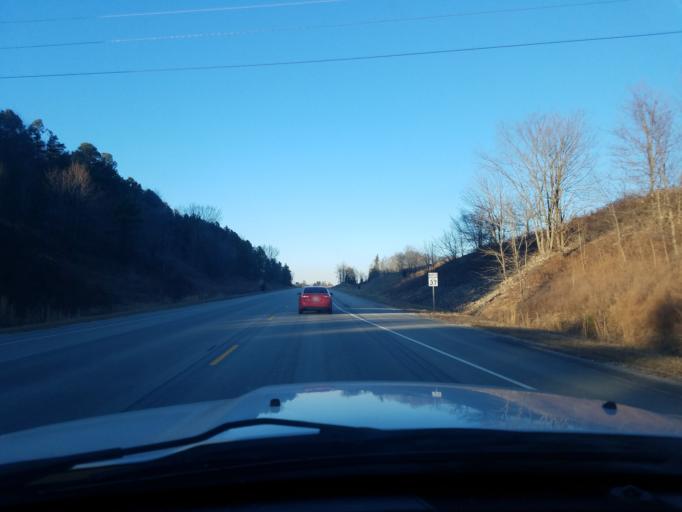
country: US
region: Indiana
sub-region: Crawford County
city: English
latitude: 38.1994
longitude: -86.5980
